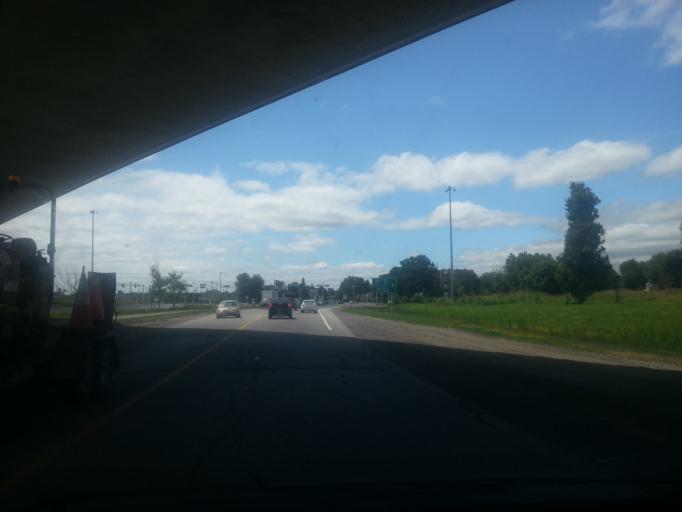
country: CA
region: Quebec
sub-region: Outaouais
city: Gatineau
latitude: 45.4710
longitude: -75.7142
